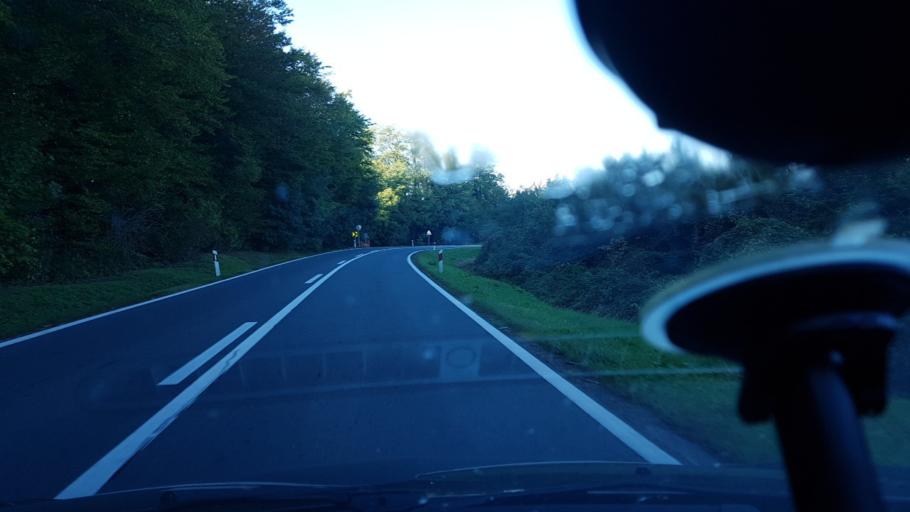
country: HR
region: Bjelovarsko-Bilogorska
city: Bjelovar
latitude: 45.9616
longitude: 16.8920
